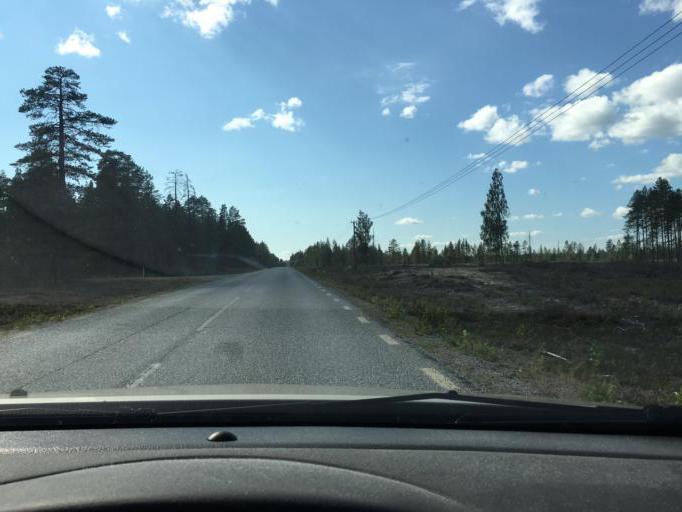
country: SE
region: Norrbotten
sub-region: Kalix Kommun
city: Toere
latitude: 66.0533
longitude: 22.5157
